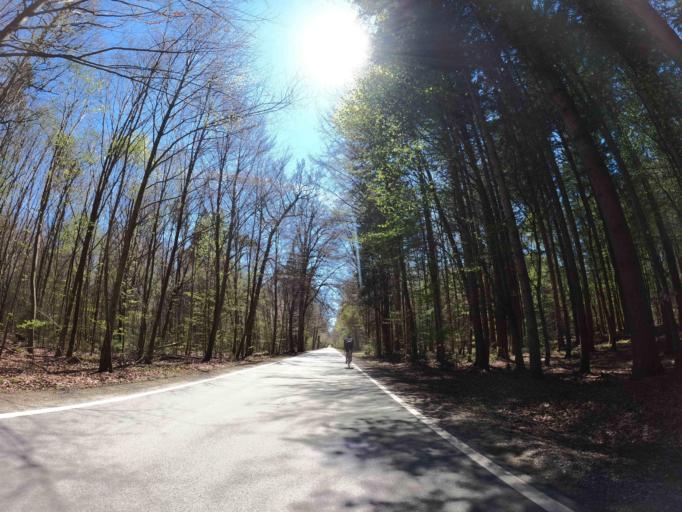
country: DE
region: Bavaria
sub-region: Upper Bavaria
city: Oberhaching
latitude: 48.0078
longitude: 11.5659
